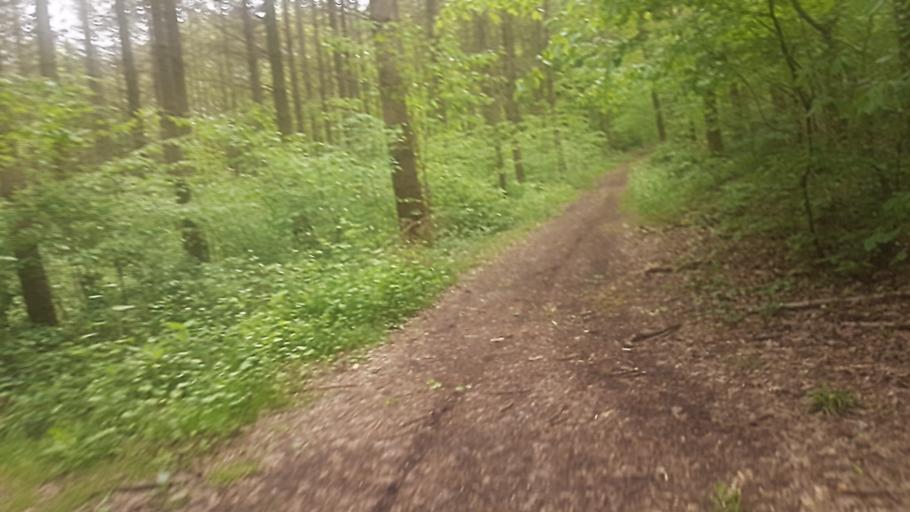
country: BE
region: Wallonia
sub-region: Province de Namur
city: Couvin
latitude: 50.0603
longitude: 4.6030
